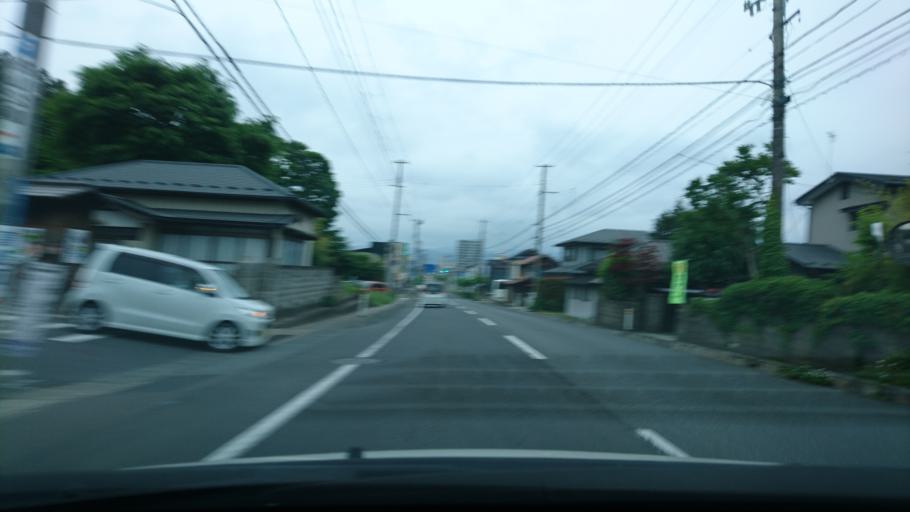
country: JP
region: Iwate
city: Ichinoseki
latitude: 38.9213
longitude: 141.1328
